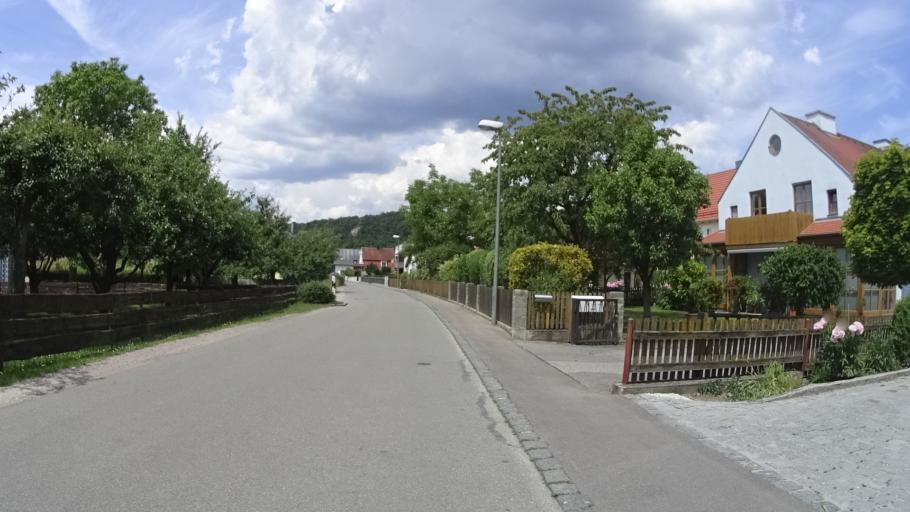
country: DE
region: Bavaria
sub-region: Lower Bavaria
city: Bad Abbach
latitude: 48.9483
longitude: 12.0165
